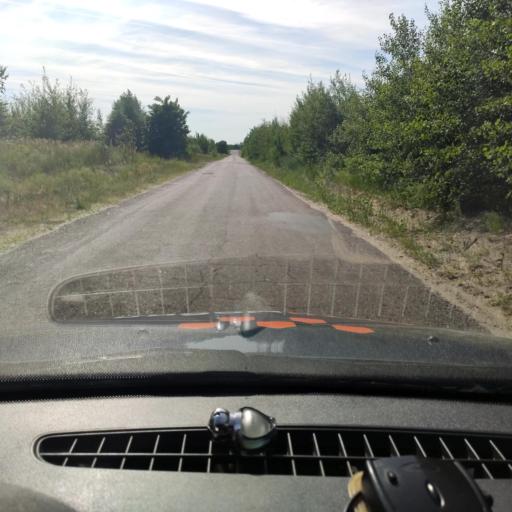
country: RU
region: Voronezj
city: Somovo
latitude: 51.7822
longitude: 39.3858
